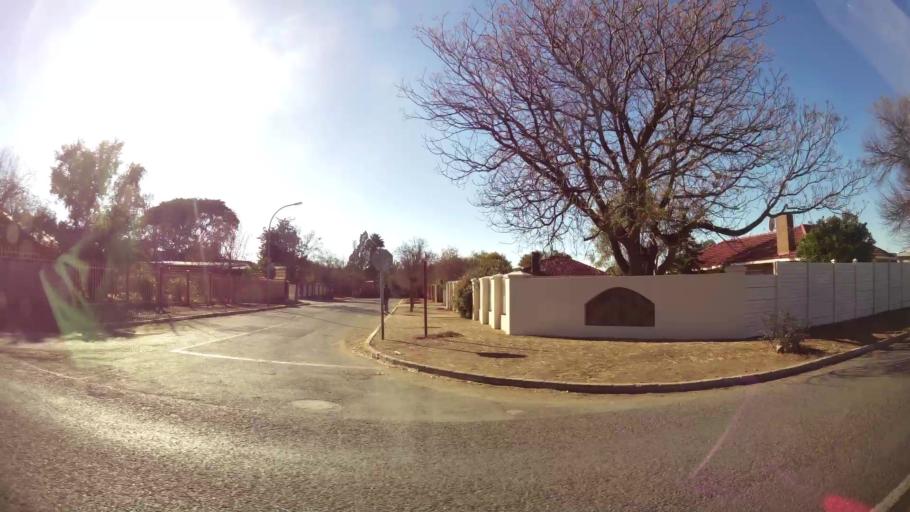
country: ZA
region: Northern Cape
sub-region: Frances Baard District Municipality
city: Kimberley
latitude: -28.7443
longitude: 24.7919
